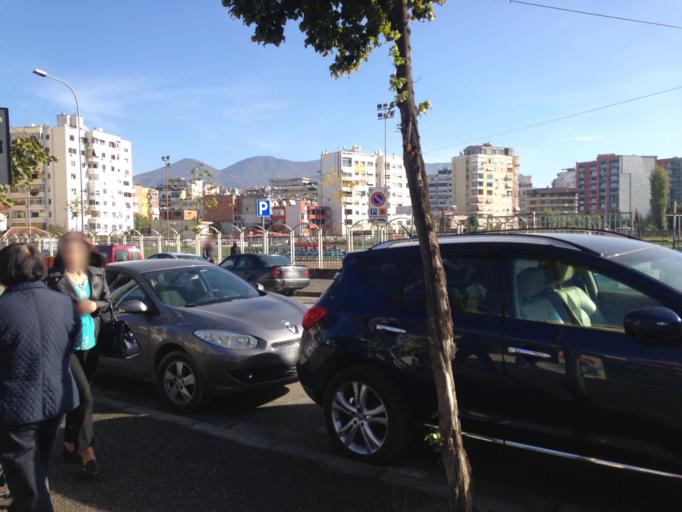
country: AL
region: Tirane
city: Tirana
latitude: 41.3147
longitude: 19.8090
